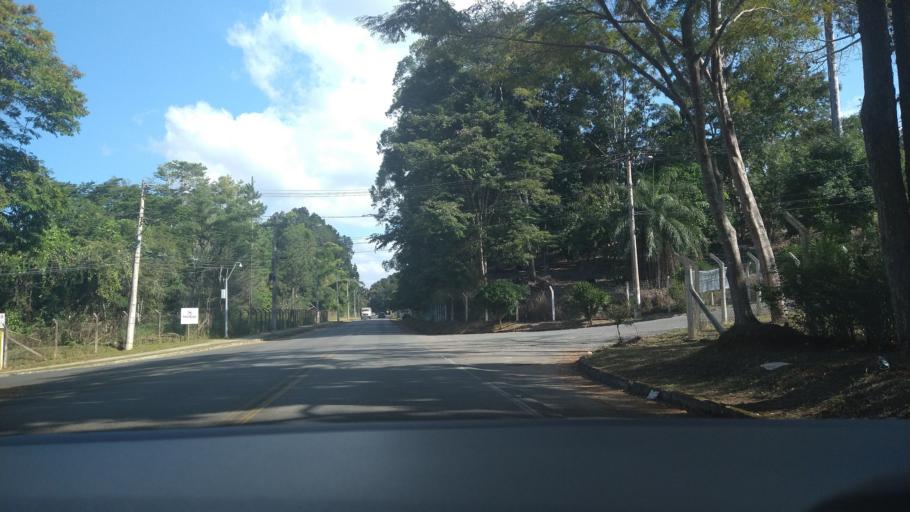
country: BR
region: Minas Gerais
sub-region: Vicosa
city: Vicosa
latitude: -20.7702
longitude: -42.8748
